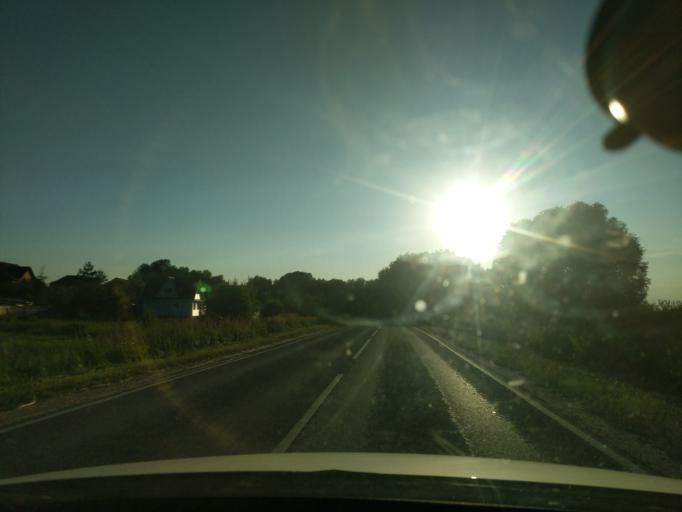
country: RU
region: Moskovskaya
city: Pushchino
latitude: 54.8445
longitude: 37.5317
